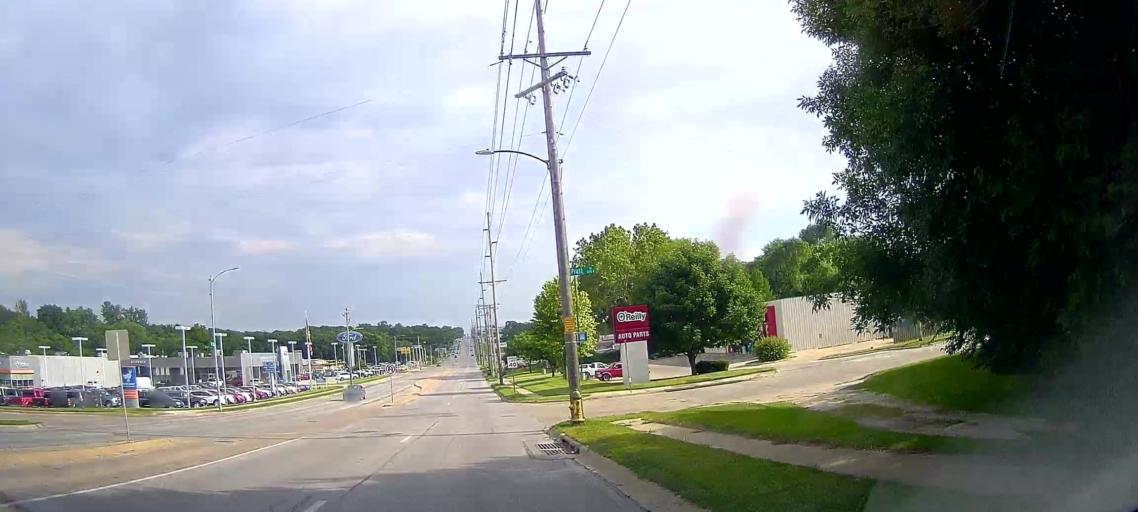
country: US
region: Nebraska
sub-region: Douglas County
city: Ralston
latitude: 41.2927
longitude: -96.0240
